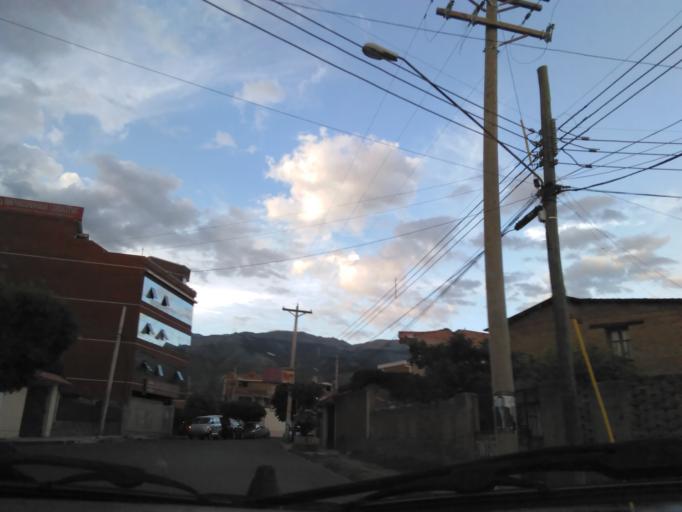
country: BO
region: Cochabamba
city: Cochabamba
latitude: -17.3880
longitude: -66.1748
